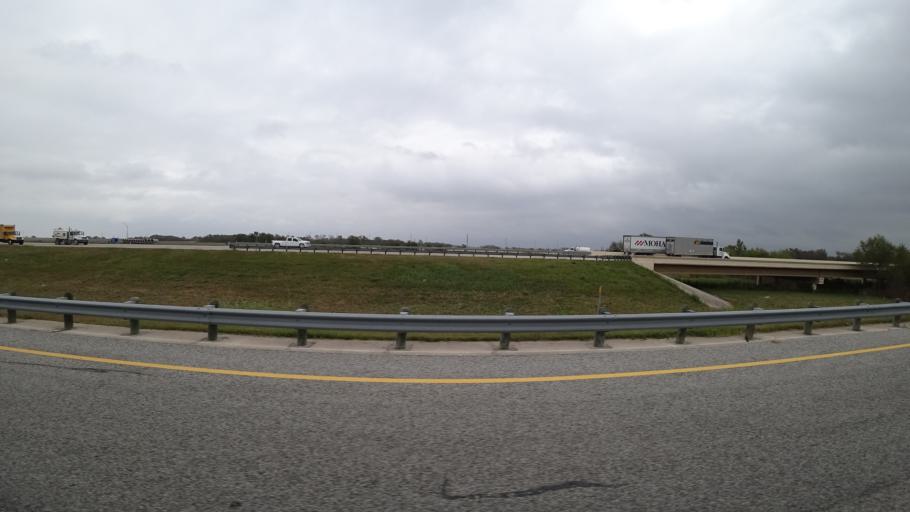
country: US
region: Texas
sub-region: Travis County
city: Pflugerville
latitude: 30.4301
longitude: -97.5906
